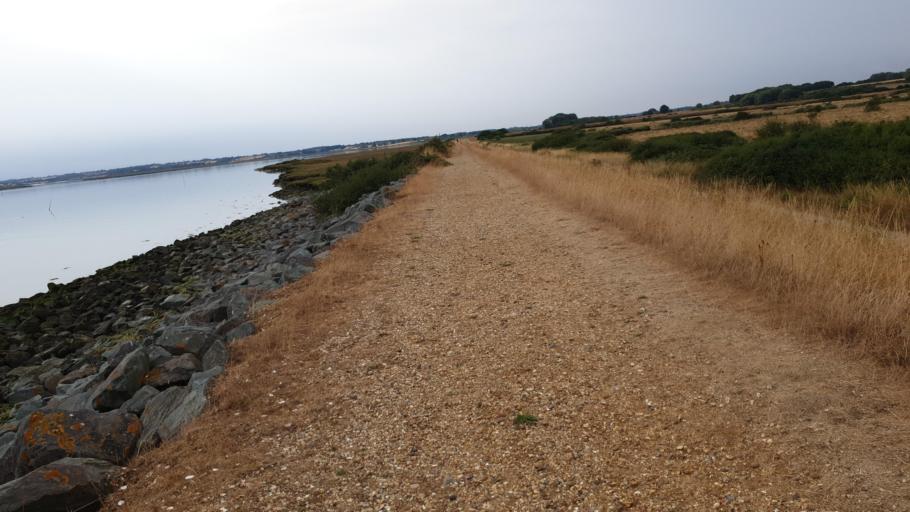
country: GB
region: England
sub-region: Essex
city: Brightlingsea
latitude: 51.8113
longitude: 1.0028
